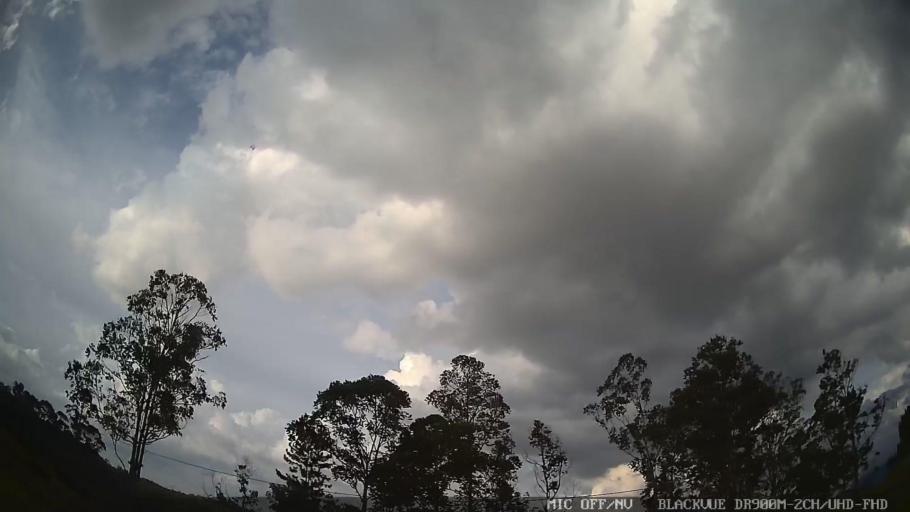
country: BR
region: Sao Paulo
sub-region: Braganca Paulista
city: Braganca Paulista
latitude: -22.9162
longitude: -46.4568
